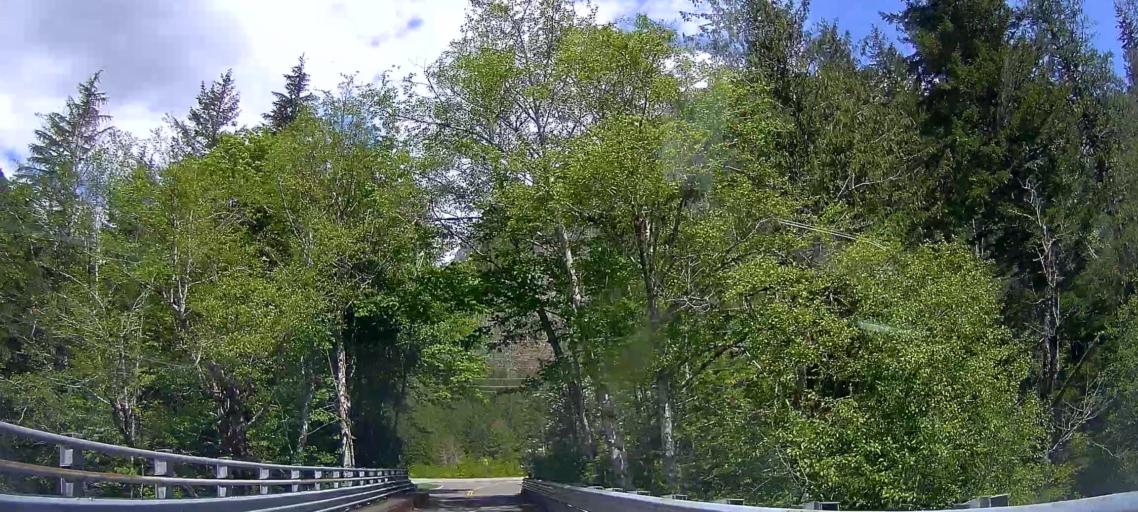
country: US
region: Washington
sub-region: Snohomish County
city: Darrington
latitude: 48.6727
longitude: -121.2615
